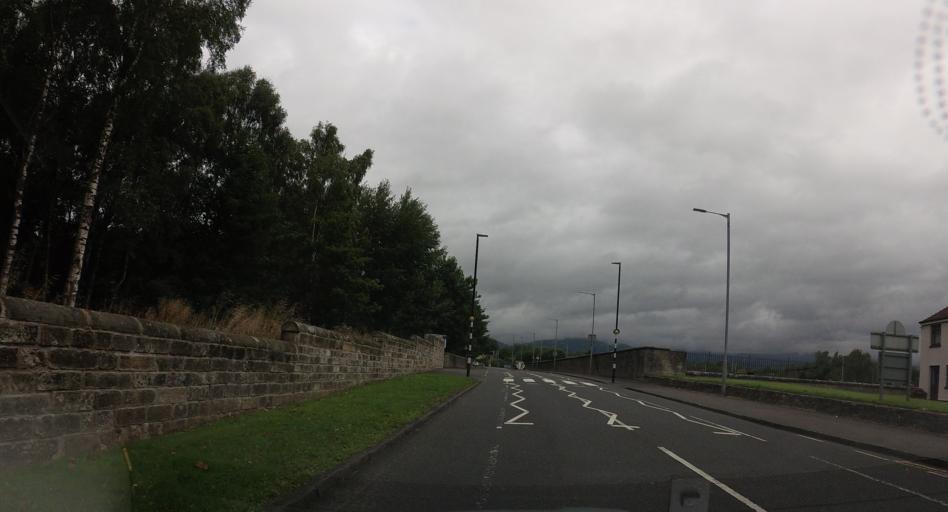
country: GB
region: Scotland
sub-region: Clackmannanshire
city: Clackmannan
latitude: 56.1124
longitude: -3.7572
